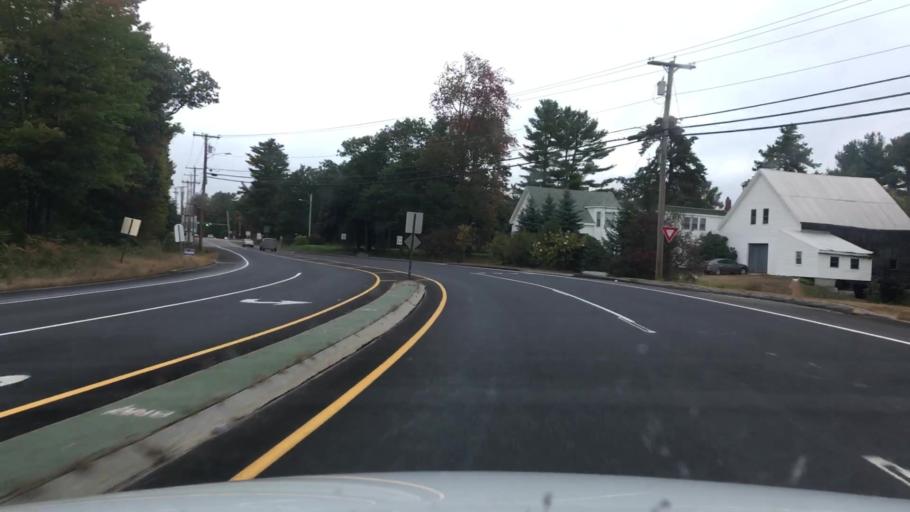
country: US
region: Maine
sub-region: Cumberland County
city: New Gloucester
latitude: 43.8994
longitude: -70.3434
